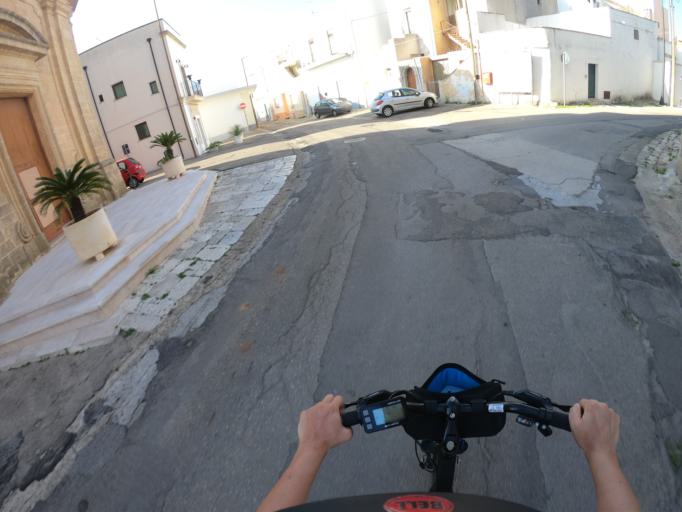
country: IT
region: Apulia
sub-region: Provincia di Lecce
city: Castrignano del Capo
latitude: 39.8332
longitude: 18.3577
